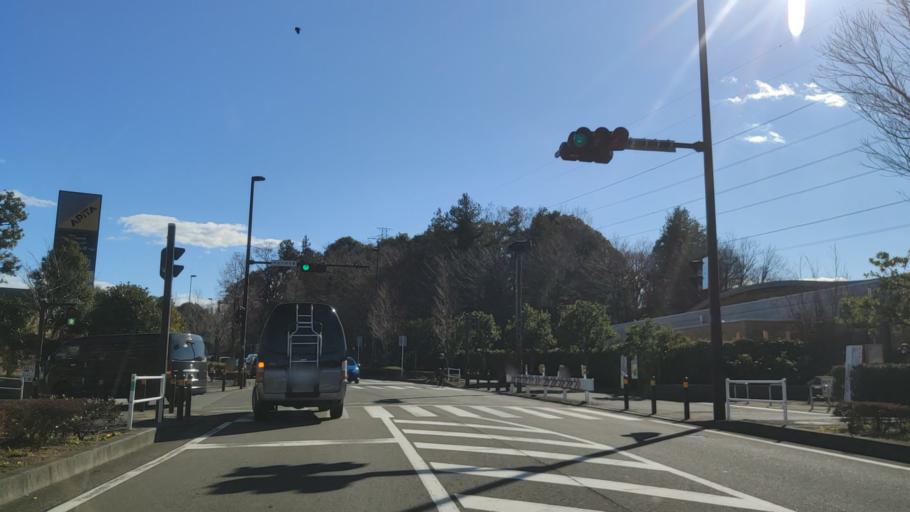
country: JP
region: Tokyo
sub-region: Machida-shi
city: Machida
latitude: 35.5187
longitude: 139.4967
